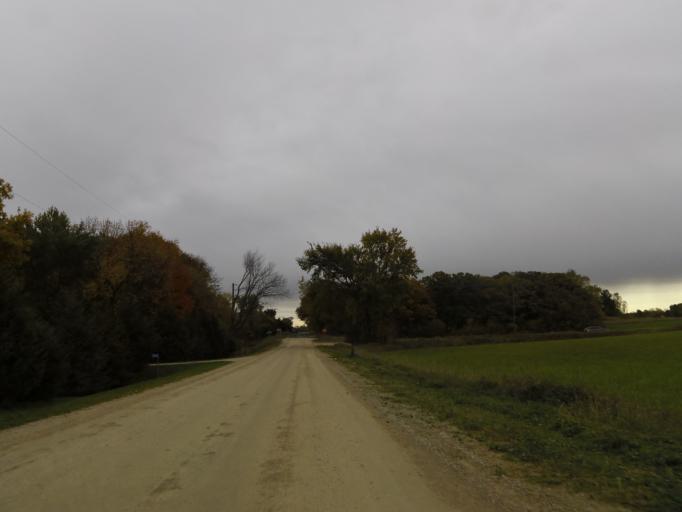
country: US
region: Minnesota
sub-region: Scott County
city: Prior Lake
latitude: 44.7036
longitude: -93.5019
